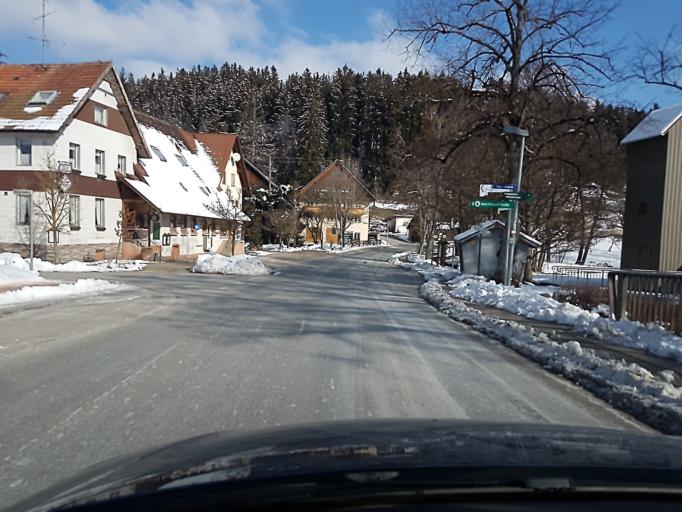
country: DE
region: Baden-Wuerttemberg
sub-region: Freiburg Region
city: Konigsfeld im Schwarzwald
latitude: 48.1513
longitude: 8.4453
